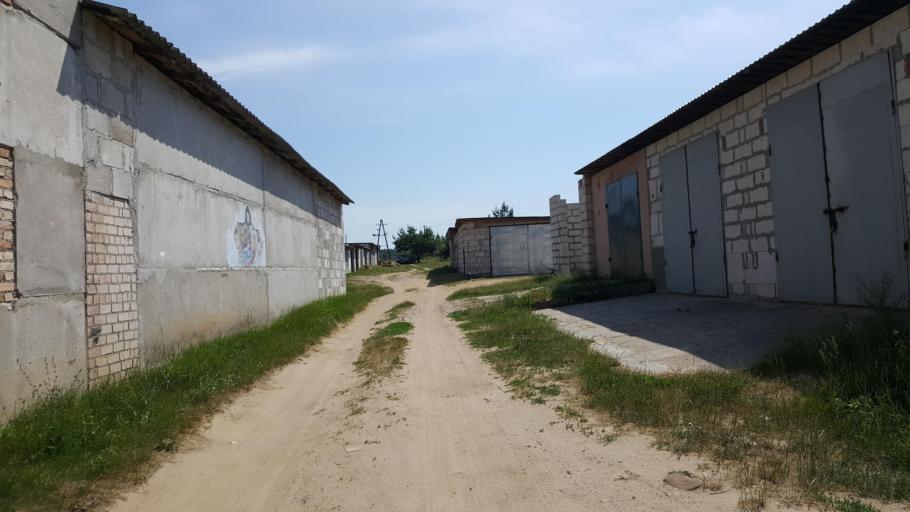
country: BY
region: Brest
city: Kamyanyets
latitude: 52.3883
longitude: 23.8263
